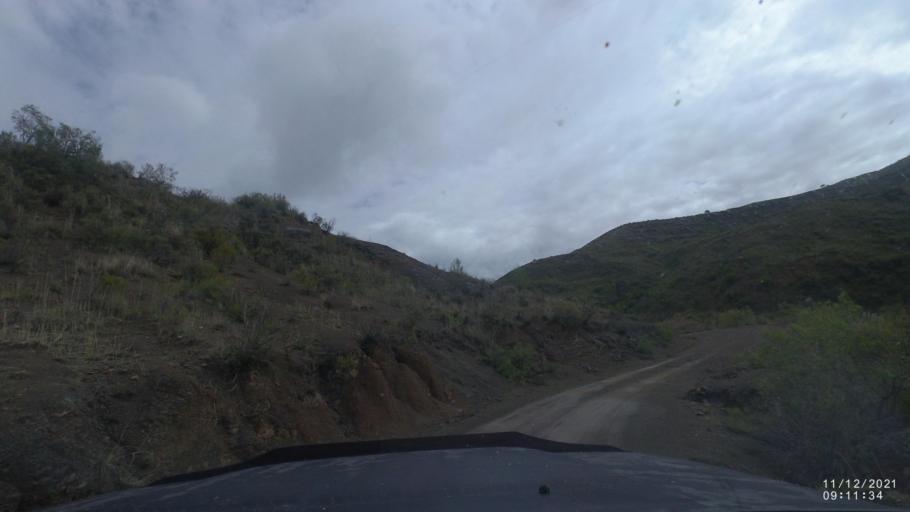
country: BO
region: Cochabamba
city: Tarata
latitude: -17.8842
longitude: -65.9614
